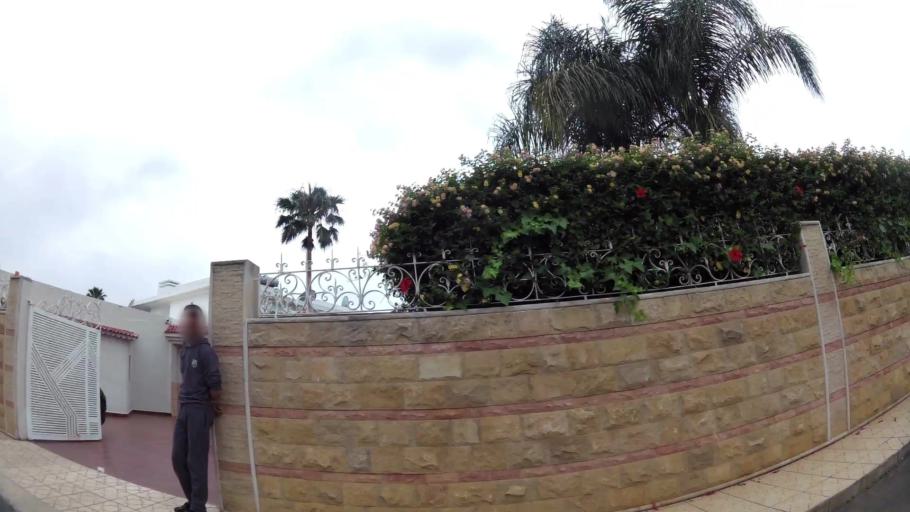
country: MA
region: Rabat-Sale-Zemmour-Zaer
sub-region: Rabat
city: Rabat
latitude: 33.9665
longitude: -6.8161
